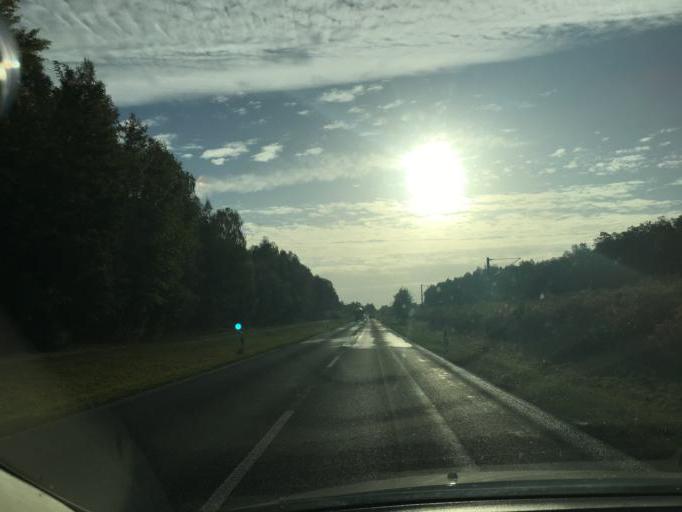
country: DE
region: Saxony
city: Lobstadt
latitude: 51.1388
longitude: 12.4348
